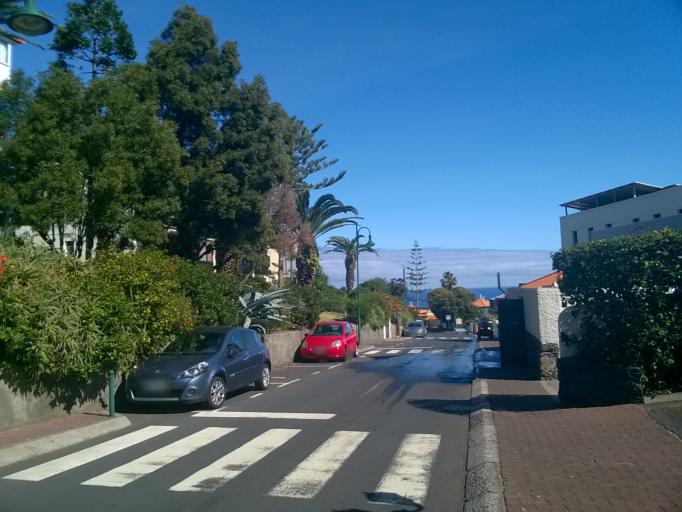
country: PT
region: Madeira
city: Canico
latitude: 32.6426
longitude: -16.8320
